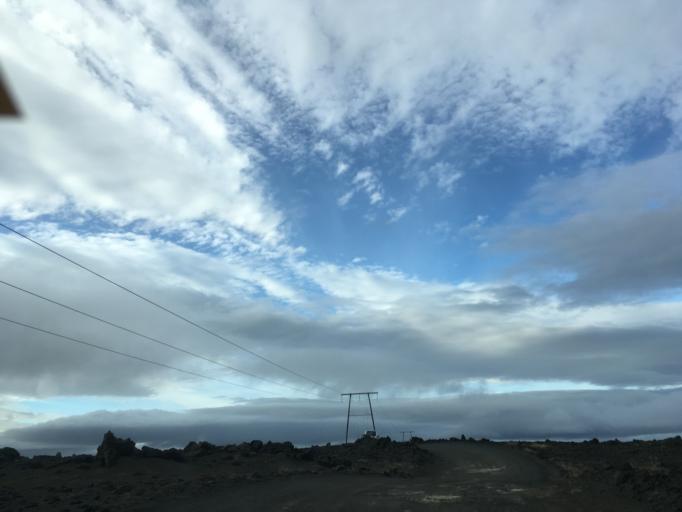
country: IS
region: South
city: Vestmannaeyjar
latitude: 64.1299
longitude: -19.1219
